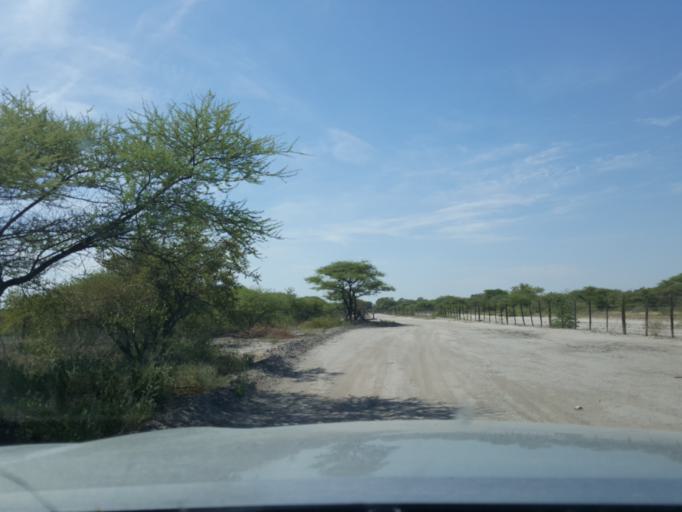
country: BW
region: North West
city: Shakawe
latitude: -18.7807
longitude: 21.7375
